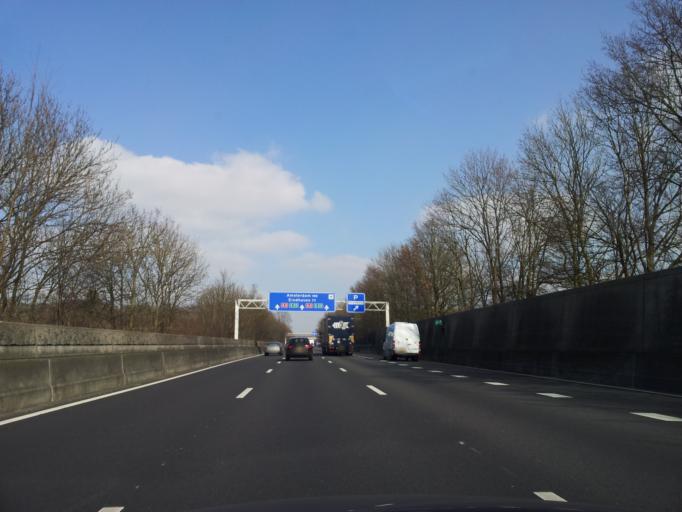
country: NL
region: Limburg
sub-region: Gemeente Meerssen
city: Meerssen
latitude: 50.8930
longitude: 5.7462
